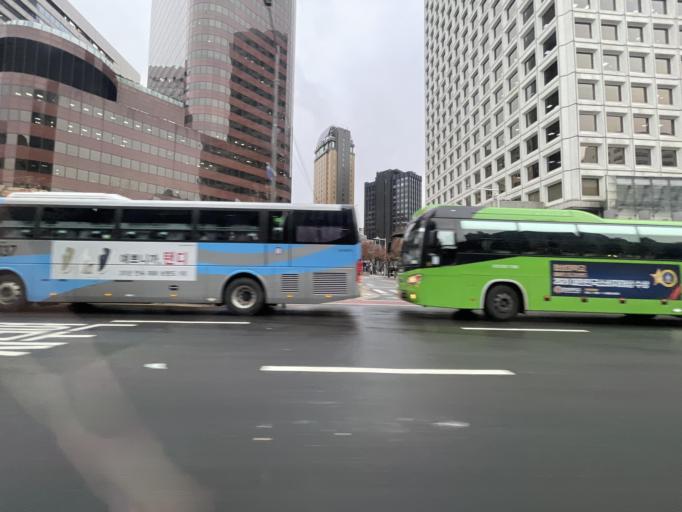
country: KR
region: Seoul
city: Seoul
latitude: 37.5618
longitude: 126.9760
